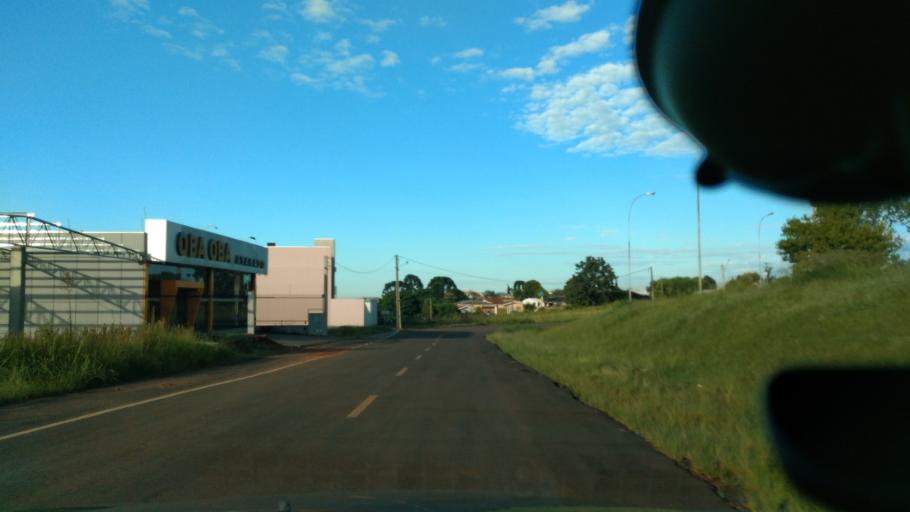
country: BR
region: Parana
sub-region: Guarapuava
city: Guarapuava
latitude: -25.3790
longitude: -51.4777
